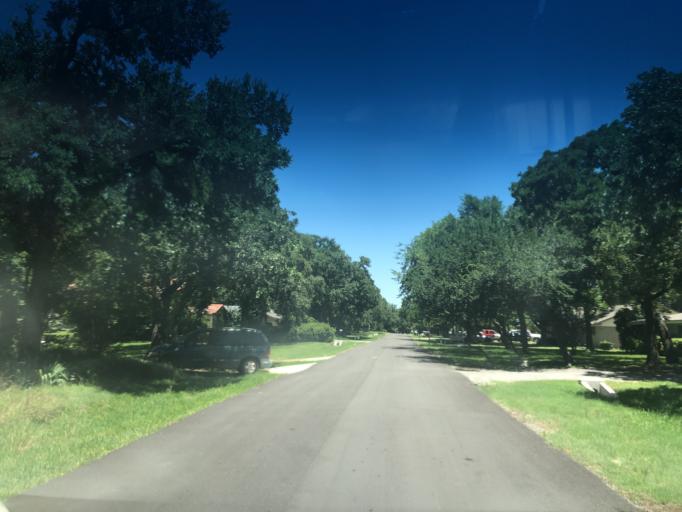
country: US
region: Texas
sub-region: Dallas County
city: Grand Prairie
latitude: 32.7775
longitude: -97.0346
